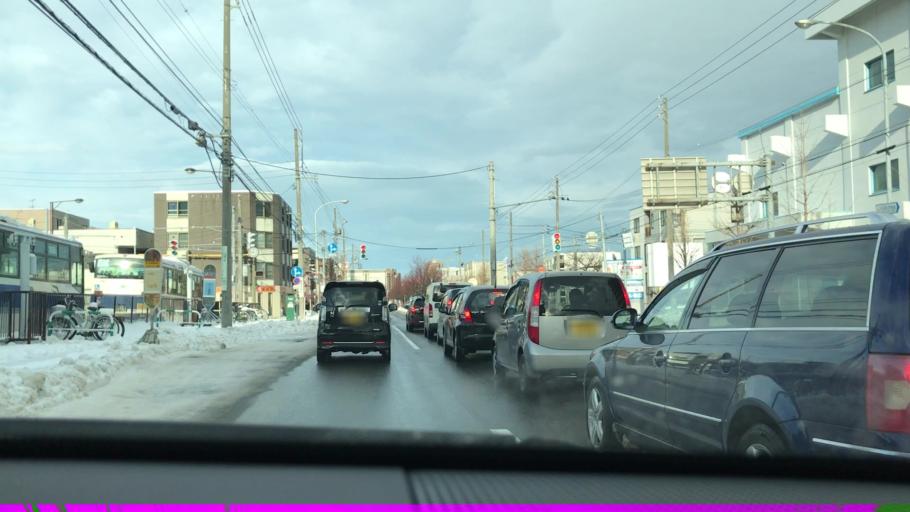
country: JP
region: Hokkaido
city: Sapporo
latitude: 43.0819
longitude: 141.2895
